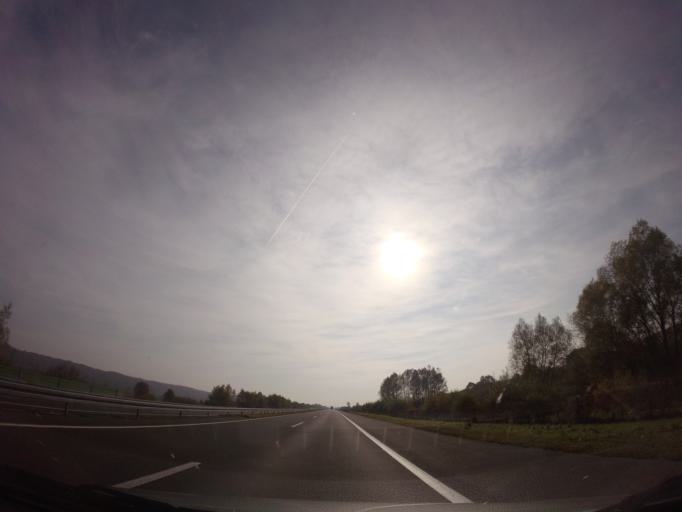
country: HR
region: Varazdinska
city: Remetinec
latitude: 46.0276
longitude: 16.2949
